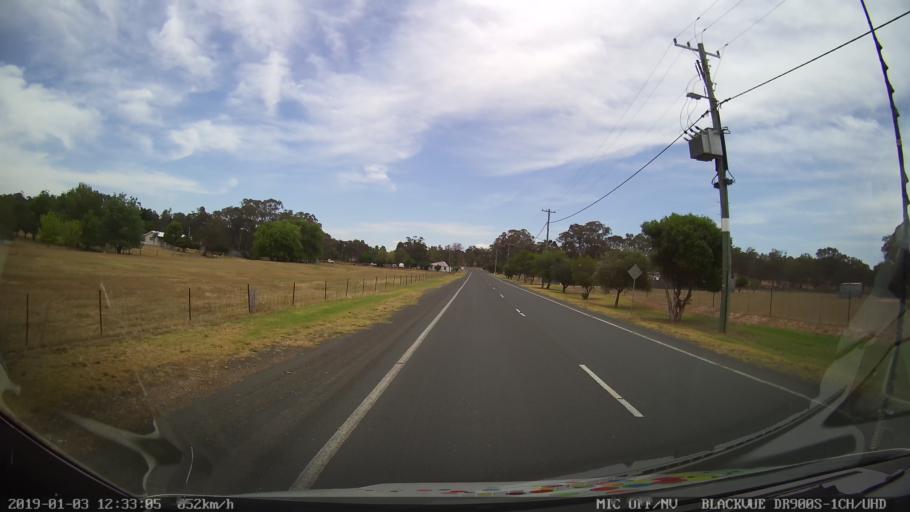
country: AU
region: New South Wales
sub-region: Weddin
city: Grenfell
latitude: -33.8879
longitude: 148.1627
